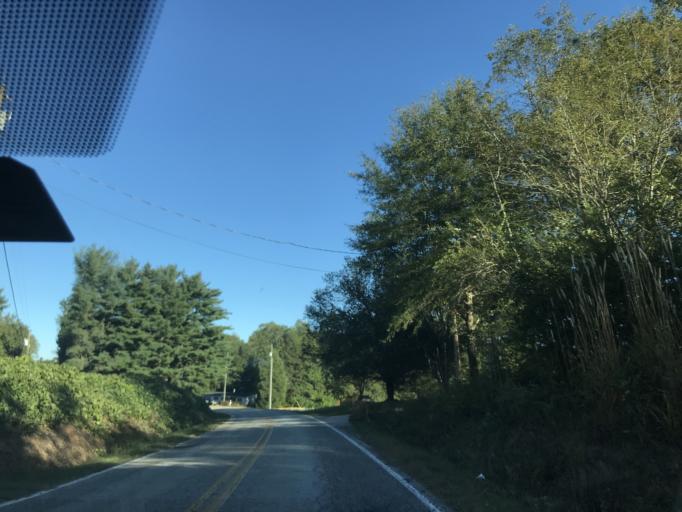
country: US
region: South Carolina
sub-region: Spartanburg County
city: Mayo
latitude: 35.1122
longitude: -81.8173
